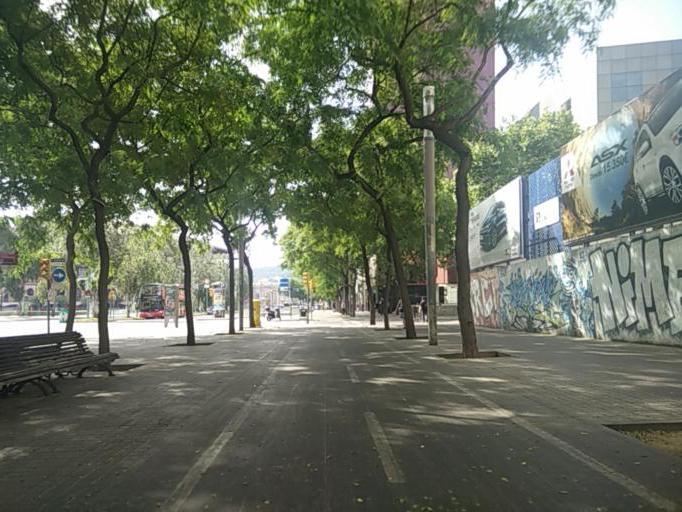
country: ES
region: Catalonia
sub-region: Provincia de Barcelona
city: Sants-Montjuic
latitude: 41.3773
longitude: 2.1465
